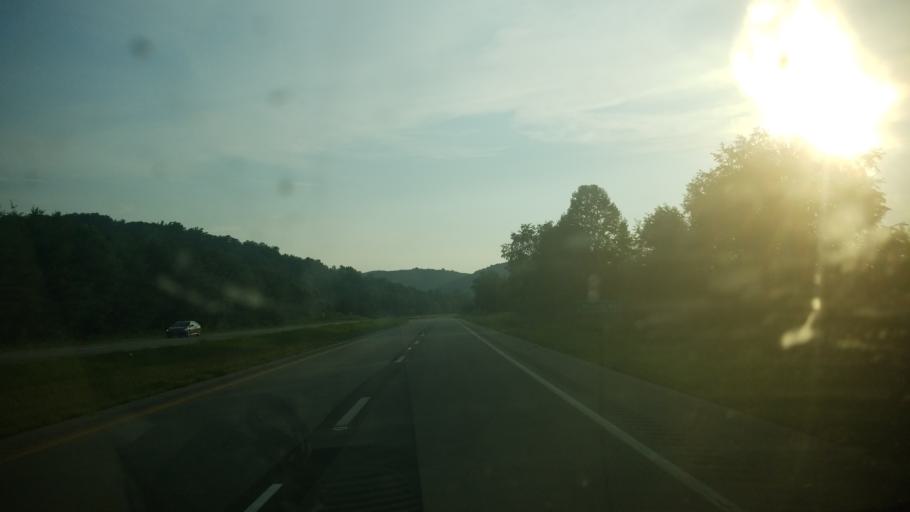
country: US
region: Ohio
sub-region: Pike County
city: Piketon
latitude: 39.0430
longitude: -83.1539
